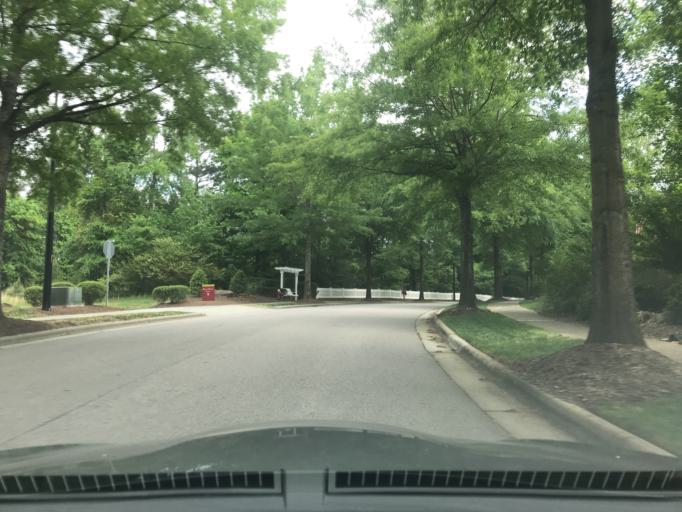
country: US
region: North Carolina
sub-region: Wake County
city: Wake Forest
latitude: 35.9288
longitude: -78.5597
